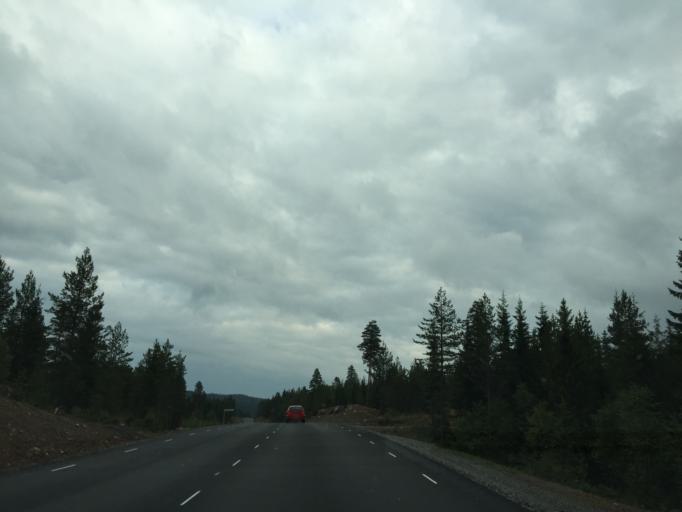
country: NO
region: Hedmark
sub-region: Loten
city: Loten
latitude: 60.6281
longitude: 11.4404
